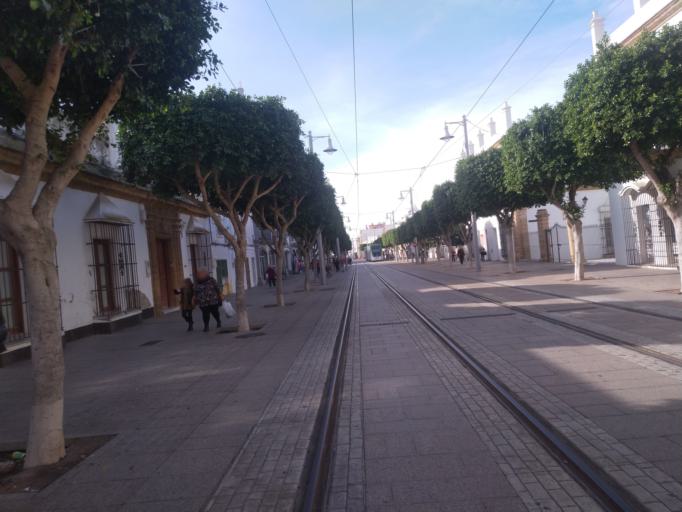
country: ES
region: Andalusia
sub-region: Provincia de Cadiz
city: San Fernando
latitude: 36.4575
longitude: -6.2053
